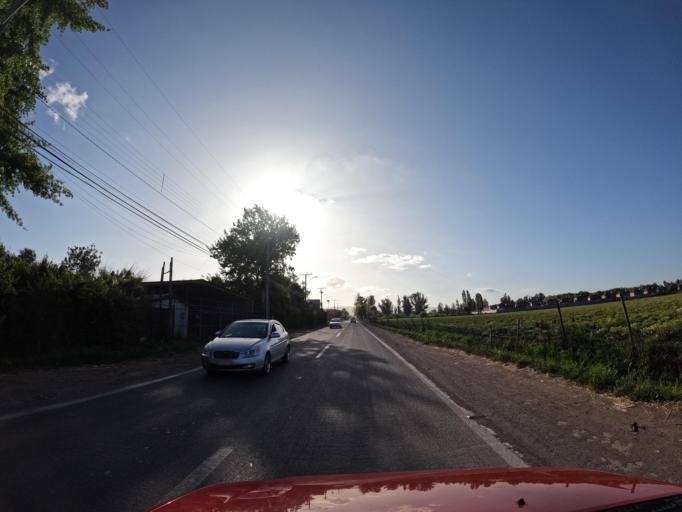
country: CL
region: O'Higgins
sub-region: Provincia de Colchagua
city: Santa Cruz
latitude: -34.6504
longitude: -71.3514
